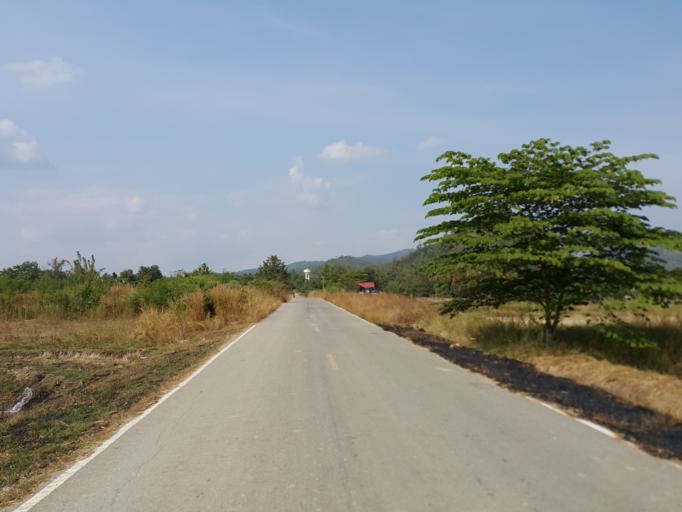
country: TH
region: Sukhothai
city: Thung Saliam
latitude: 17.3405
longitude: 99.4404
